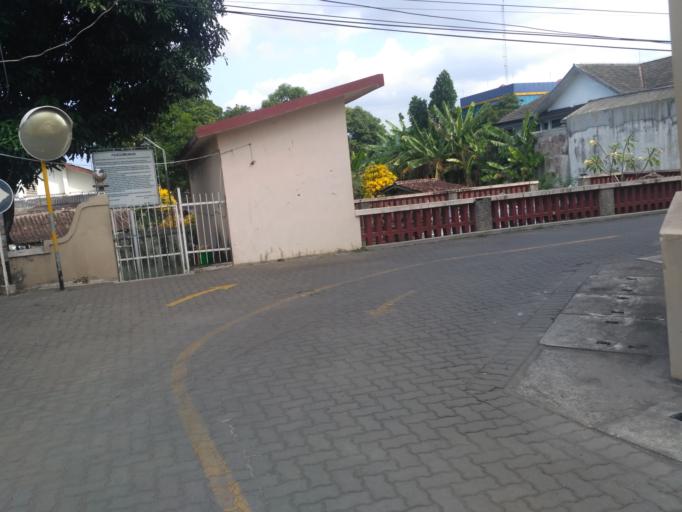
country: ID
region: Daerah Istimewa Yogyakarta
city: Depok
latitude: -7.7820
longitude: 110.4093
